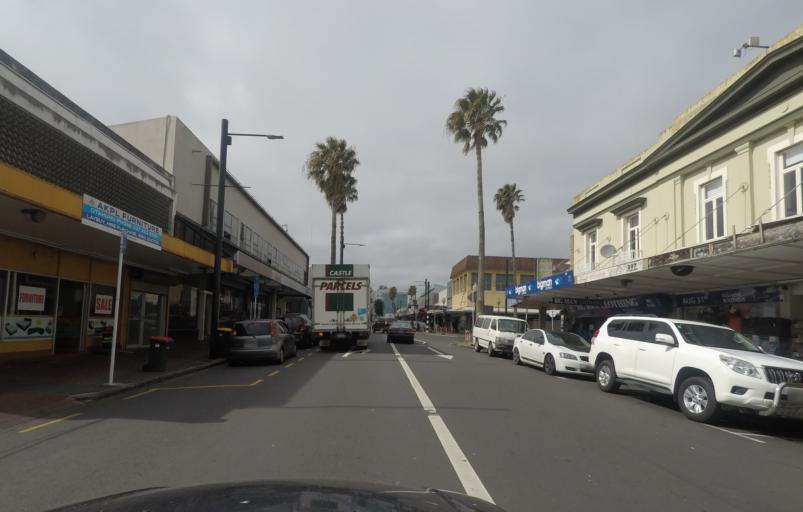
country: NZ
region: Auckland
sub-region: Auckland
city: Mangere
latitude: -36.9441
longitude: 174.8437
